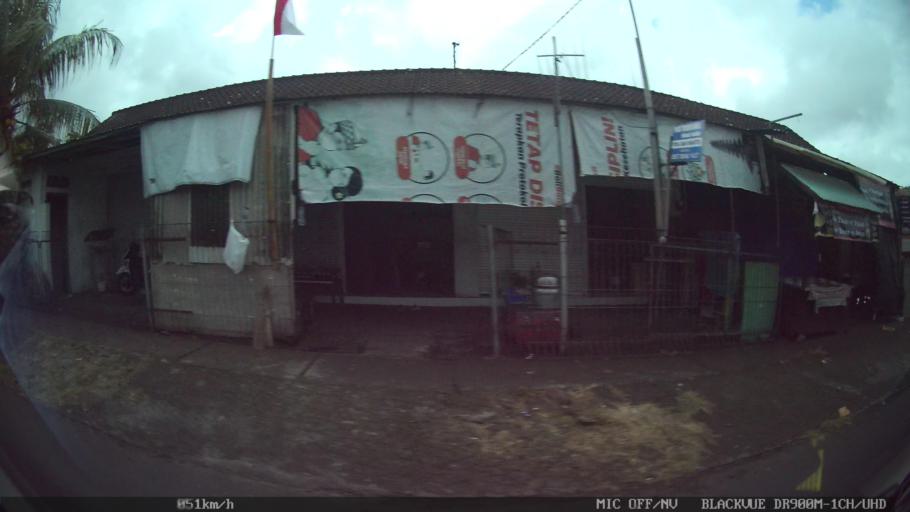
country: ID
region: Bali
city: Banjar Serangan
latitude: -8.5296
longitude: 115.1800
